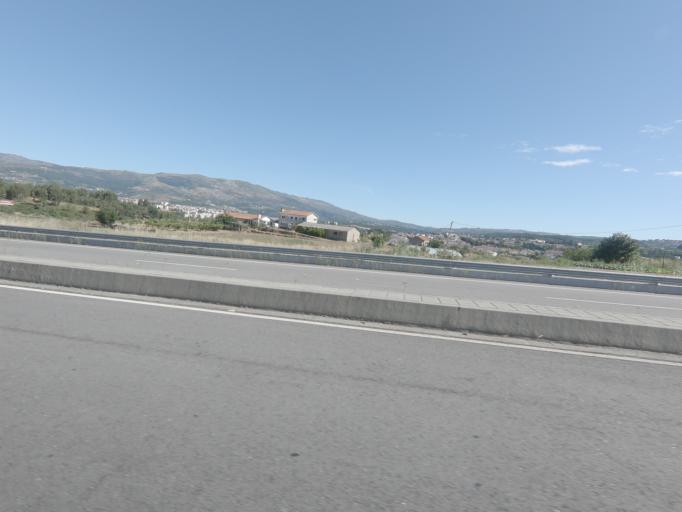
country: PT
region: Vila Real
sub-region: Vila Real
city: Vila Real
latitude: 41.2848
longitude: -7.7303
